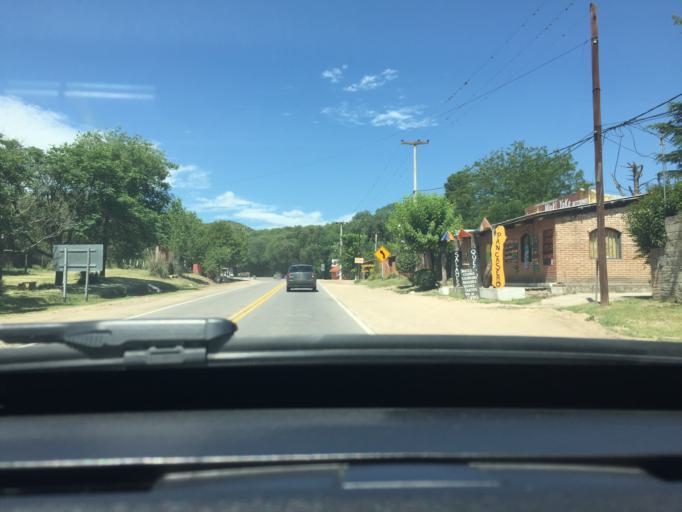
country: AR
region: Cordoba
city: Alta Gracia
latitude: -31.7362
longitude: -64.4510
